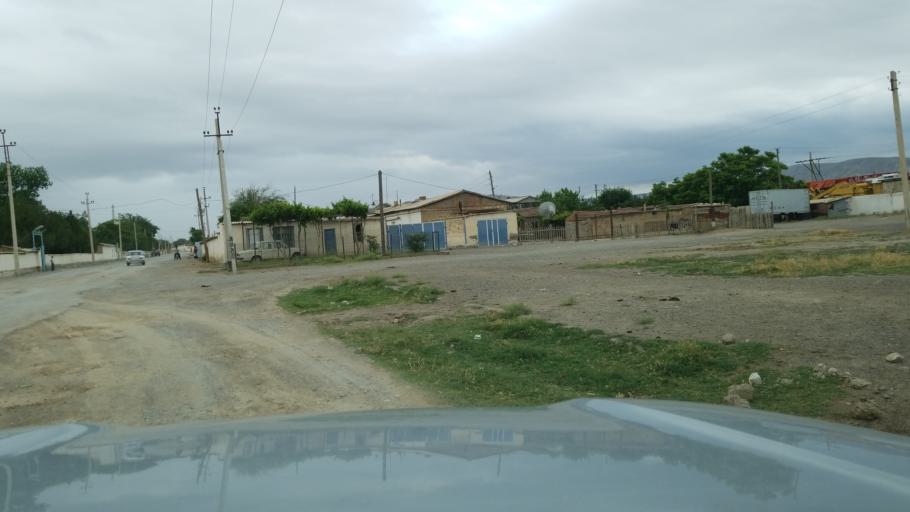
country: TM
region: Balkan
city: Serdar
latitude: 38.9829
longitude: 56.2629
